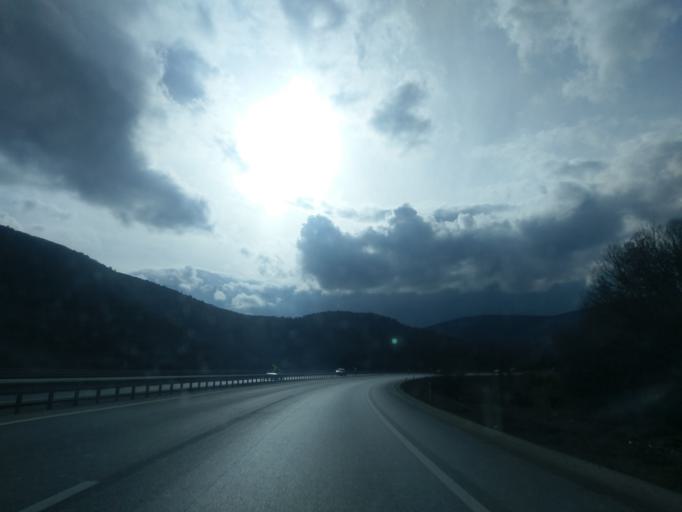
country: TR
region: Kuetahya
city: Sabuncu
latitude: 39.5586
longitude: 30.0756
